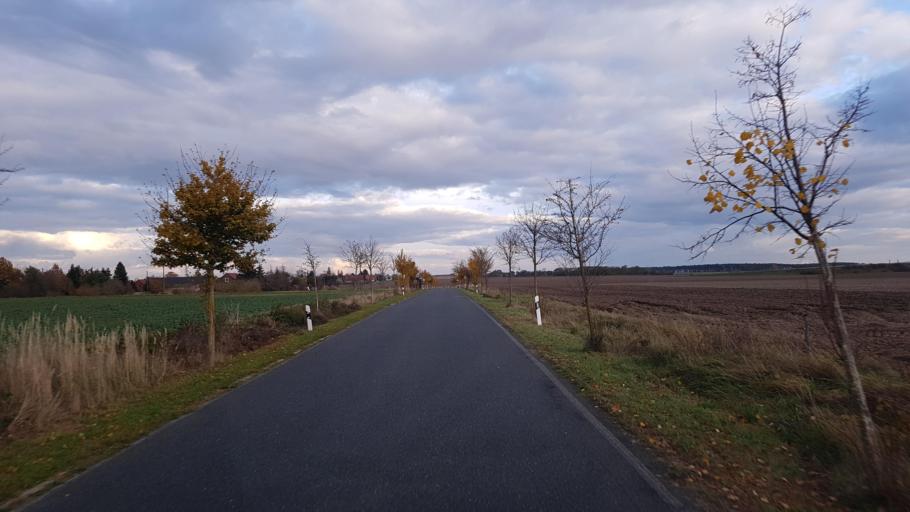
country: DE
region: Saxony-Anhalt
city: Zahna
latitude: 51.9458
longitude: 12.8250
